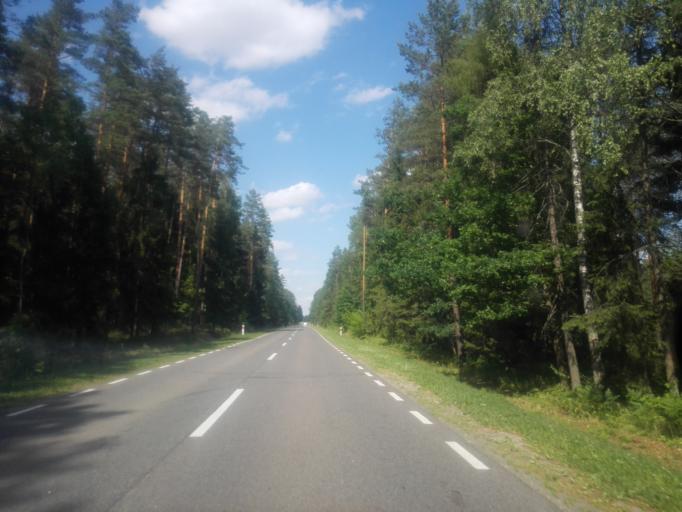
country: PL
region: Podlasie
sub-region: Powiat sejnenski
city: Sejny
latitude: 53.9879
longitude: 23.3011
